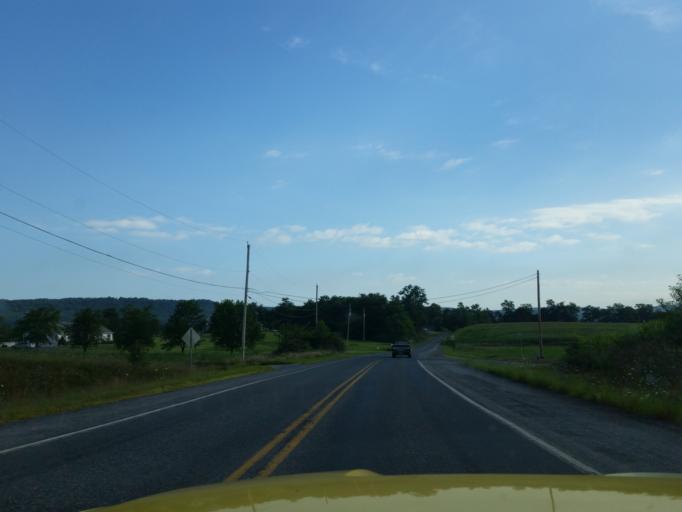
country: US
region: Pennsylvania
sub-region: Lebanon County
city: Fredericksburg
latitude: 40.4535
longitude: -76.4144
